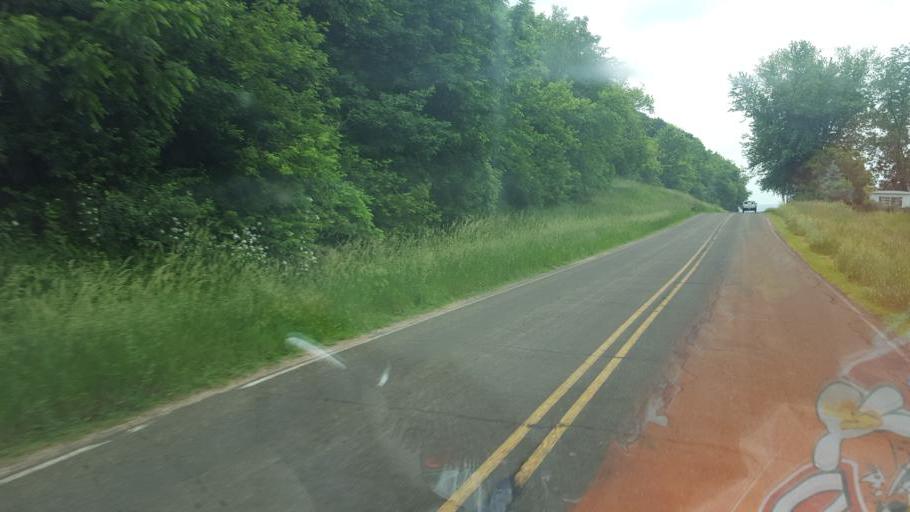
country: US
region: Wisconsin
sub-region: Vernon County
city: Hillsboro
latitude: 43.6448
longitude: -90.2881
